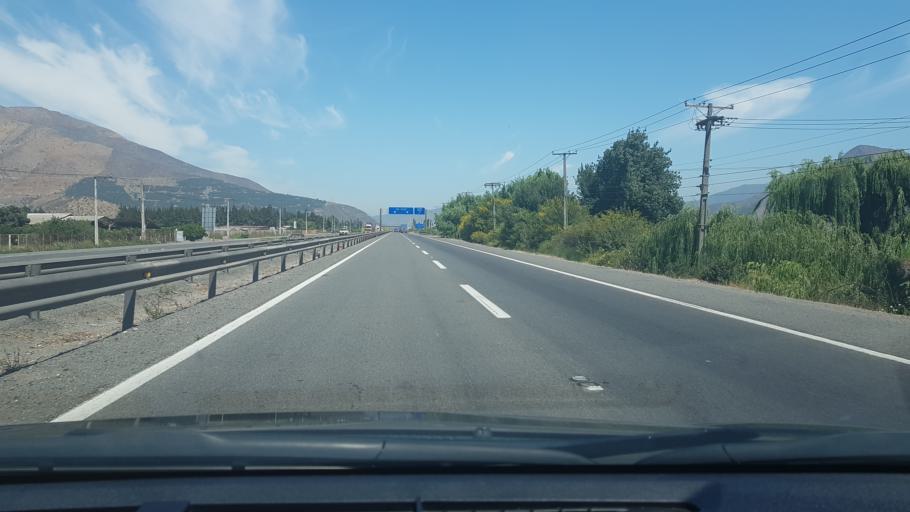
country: CL
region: Valparaiso
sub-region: Provincia de San Felipe
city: Llaillay
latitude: -32.8466
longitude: -70.9704
